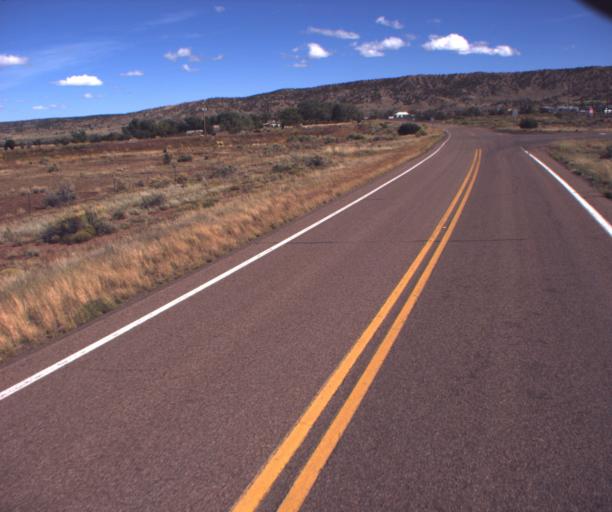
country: US
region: Arizona
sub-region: Apache County
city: Saint Johns
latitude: 34.4788
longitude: -109.6141
